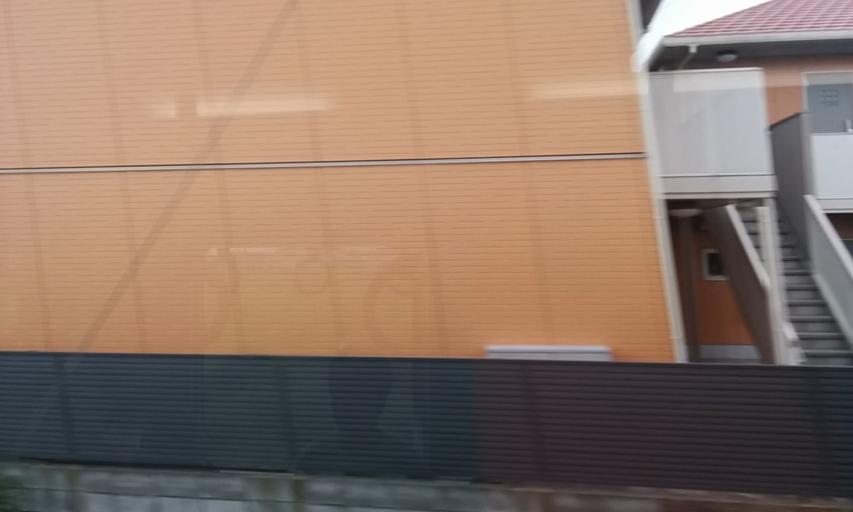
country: JP
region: Nara
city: Nara-shi
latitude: 34.6621
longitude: 135.7836
